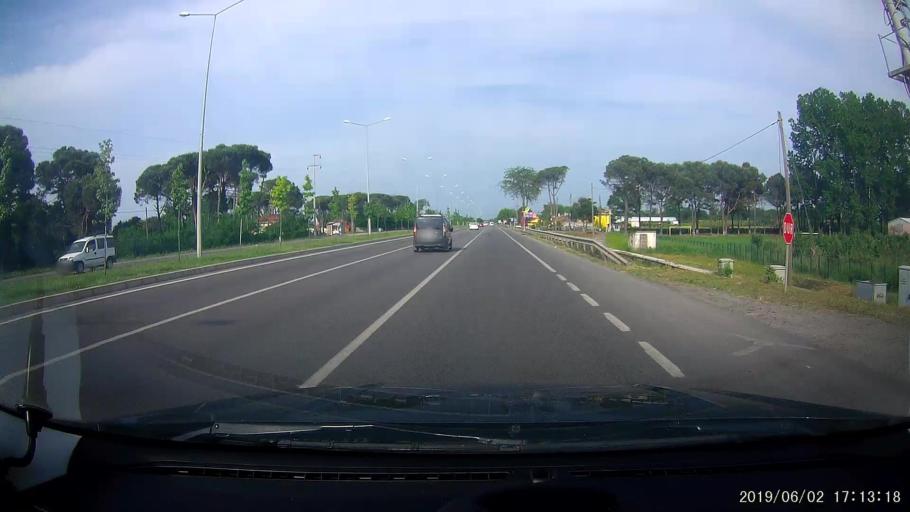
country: TR
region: Samsun
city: Tekkekoy
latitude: 41.2308
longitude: 36.5053
